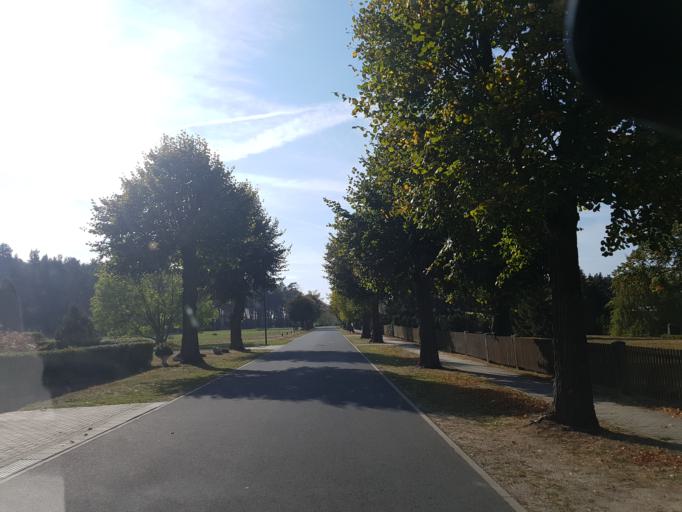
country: DE
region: Brandenburg
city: Hohenbucko
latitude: 51.7618
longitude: 13.4663
